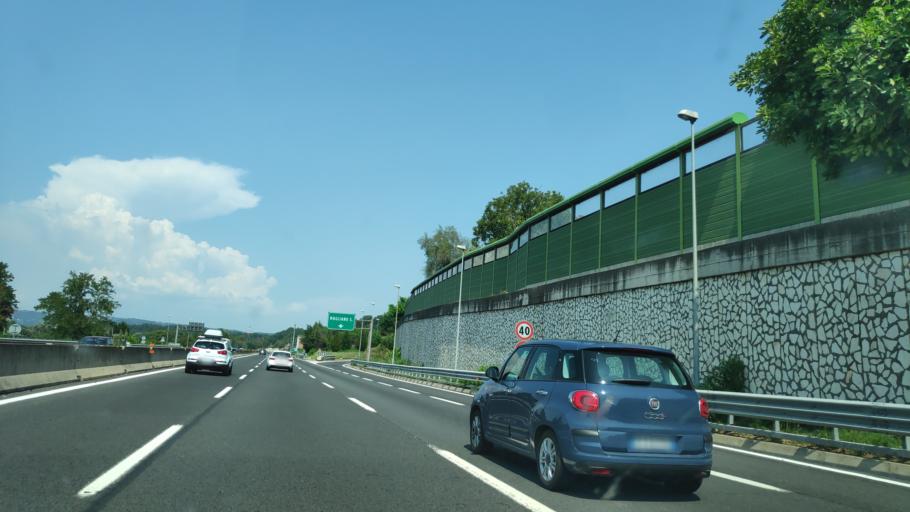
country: IT
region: Latium
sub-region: Provincia di Rieti
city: Magliano Sabina
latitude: 42.3792
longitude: 12.4719
